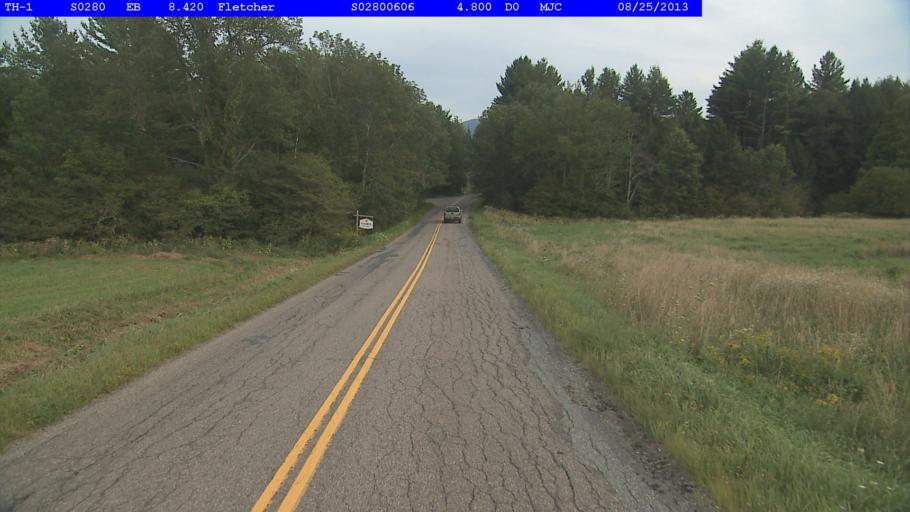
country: US
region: Vermont
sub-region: Chittenden County
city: Jericho
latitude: 44.6633
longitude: -72.8883
